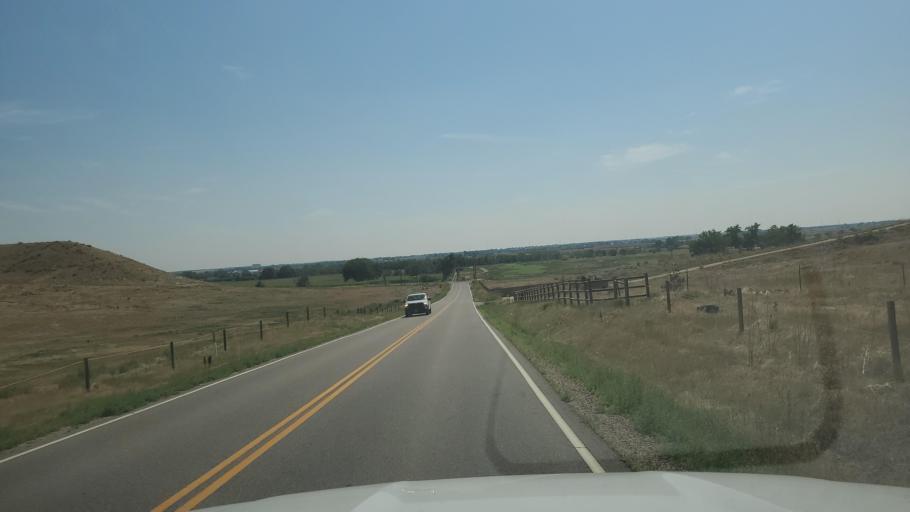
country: US
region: Colorado
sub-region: Adams County
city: Todd Creek
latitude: 39.9431
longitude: -104.8754
